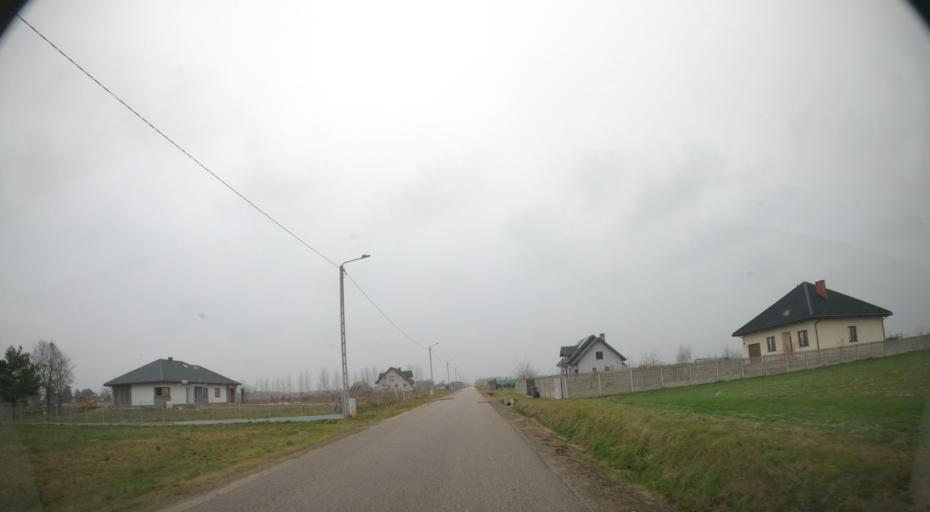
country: PL
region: Masovian Voivodeship
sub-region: Powiat radomski
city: Jedlnia-Letnisko
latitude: 51.4078
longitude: 21.2932
